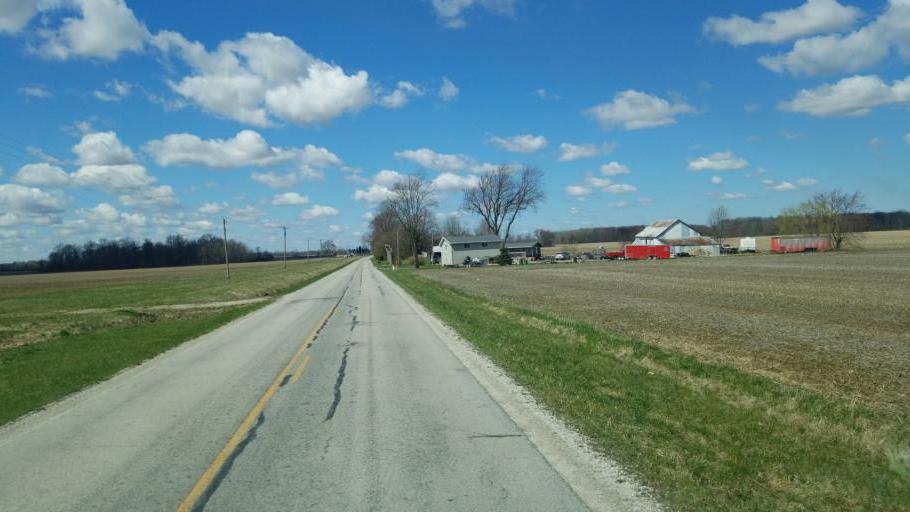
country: US
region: Ohio
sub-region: Sandusky County
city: Green Springs
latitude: 41.2423
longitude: -83.0297
